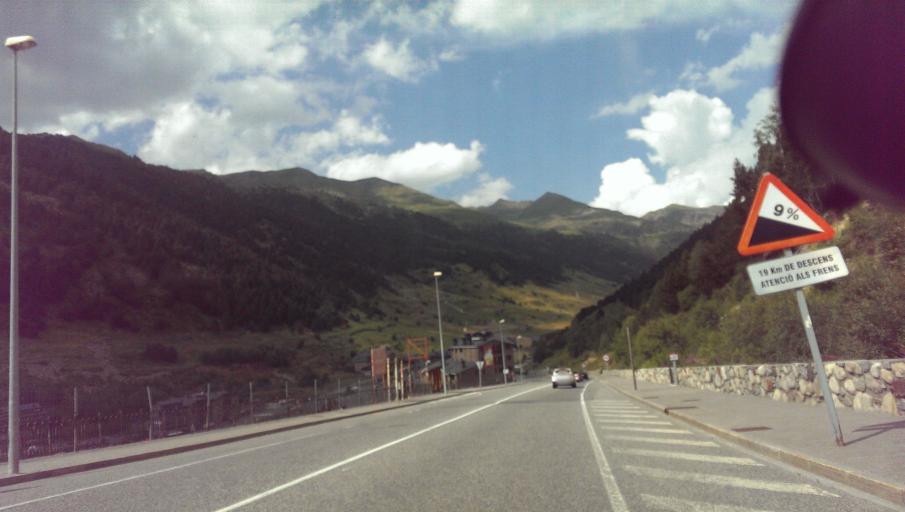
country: AD
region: Canillo
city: El Tarter
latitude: 42.5798
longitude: 1.6638
